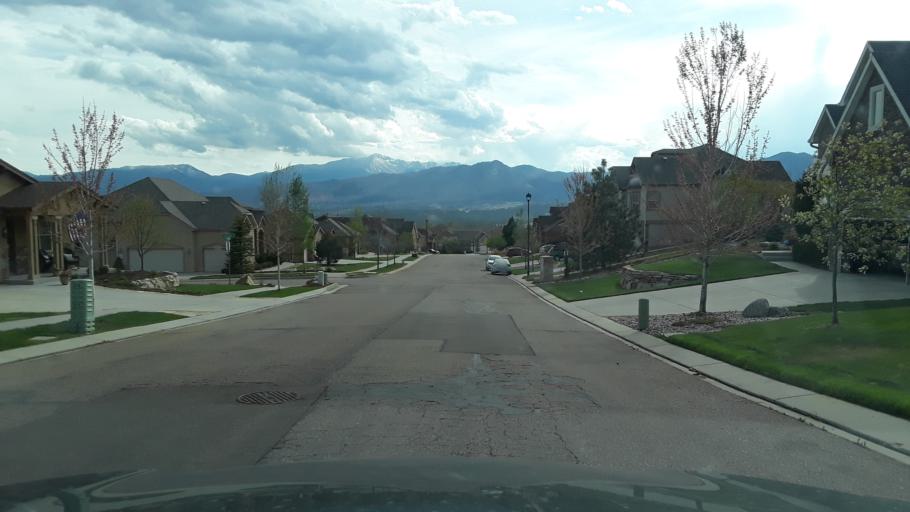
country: US
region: Colorado
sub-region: El Paso County
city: Gleneagle
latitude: 39.0143
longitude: -104.7964
